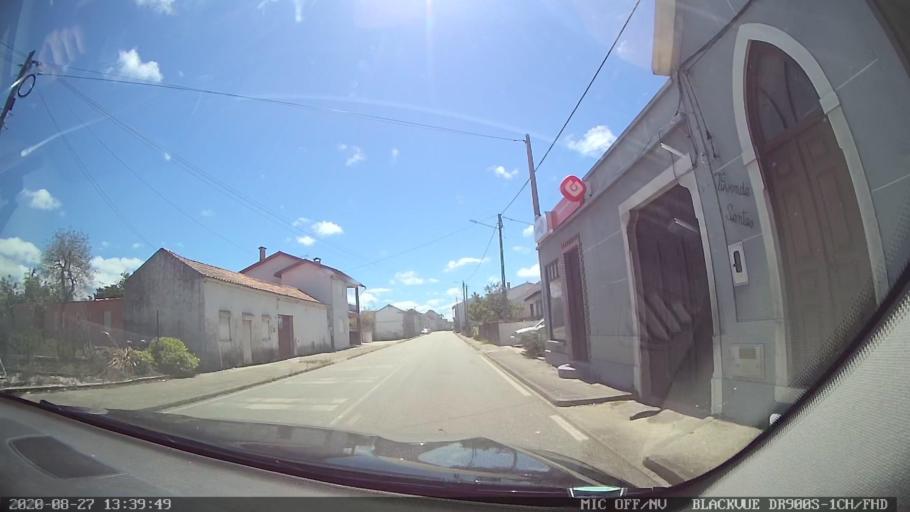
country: PT
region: Coimbra
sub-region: Mira
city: Mira
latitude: 40.4384
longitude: -8.7282
